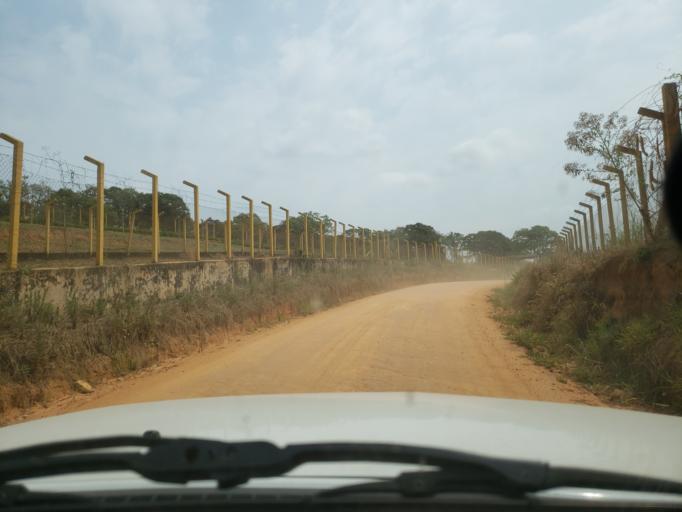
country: BR
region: Minas Gerais
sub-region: Jacutinga
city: Jacutinga
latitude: -22.3134
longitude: -46.6037
